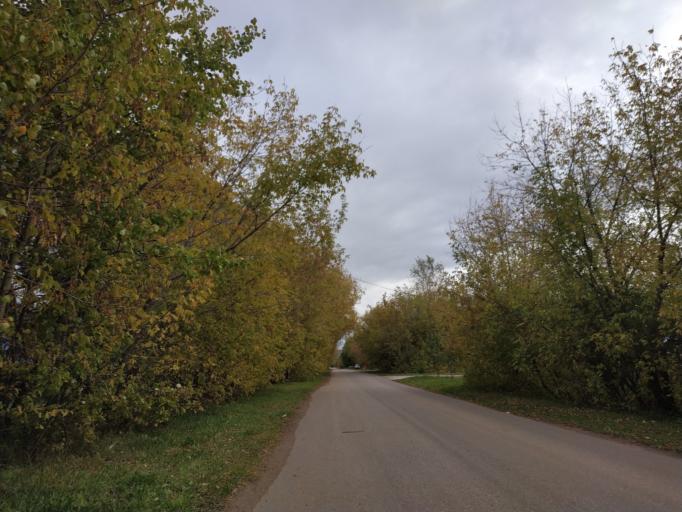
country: RU
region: Chuvashia
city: Ishley
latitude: 56.1272
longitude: 47.0917
